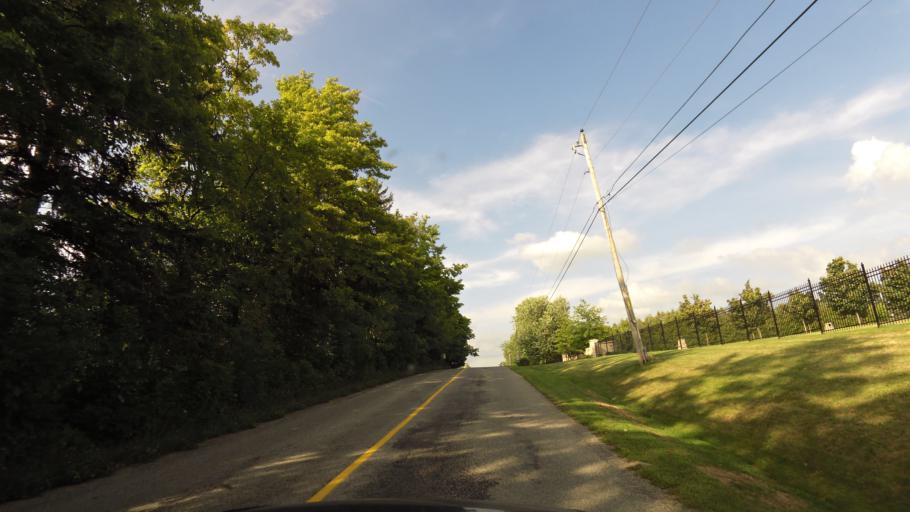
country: CA
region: Ontario
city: Burlington
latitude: 43.3836
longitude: -79.8669
